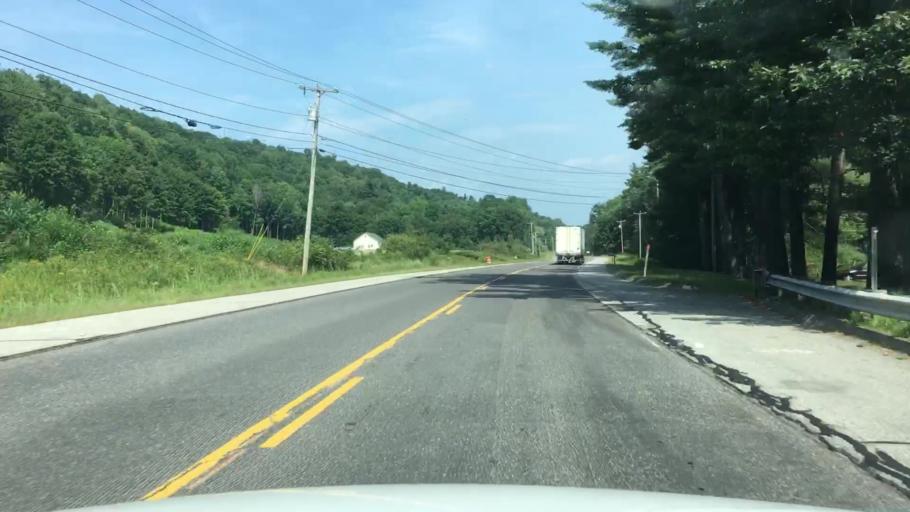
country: US
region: Maine
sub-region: Androscoggin County
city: Turner
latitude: 44.3104
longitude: -70.2655
